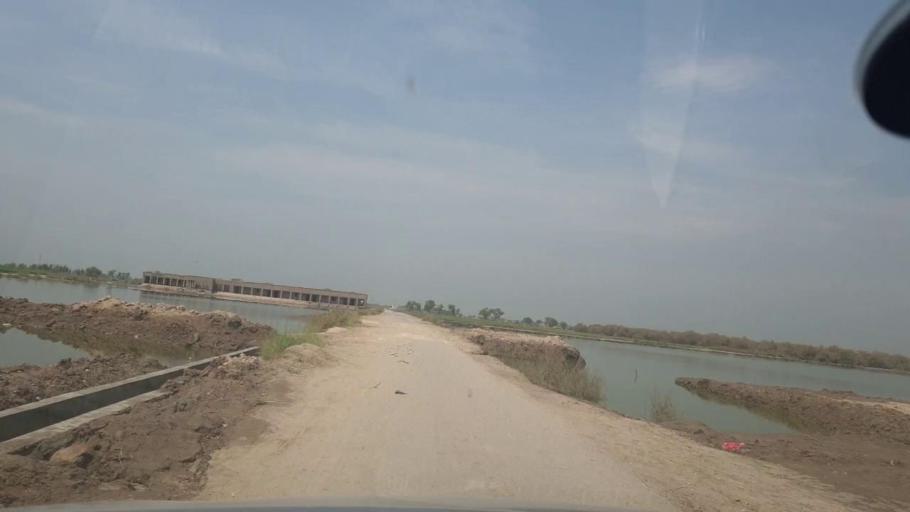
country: PK
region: Sindh
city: Thul
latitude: 28.1679
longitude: 68.6361
